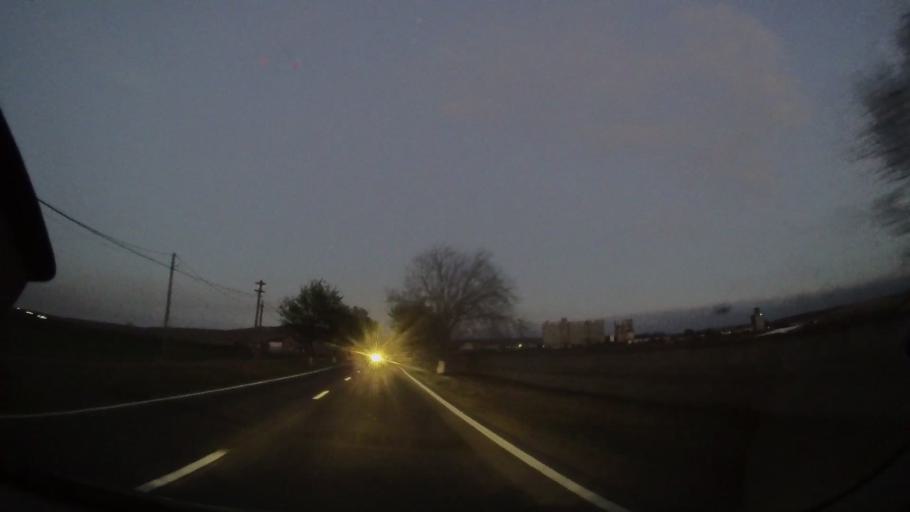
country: RO
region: Tulcea
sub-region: Comuna Frecatei
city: Cataloi
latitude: 45.1035
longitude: 28.7388
